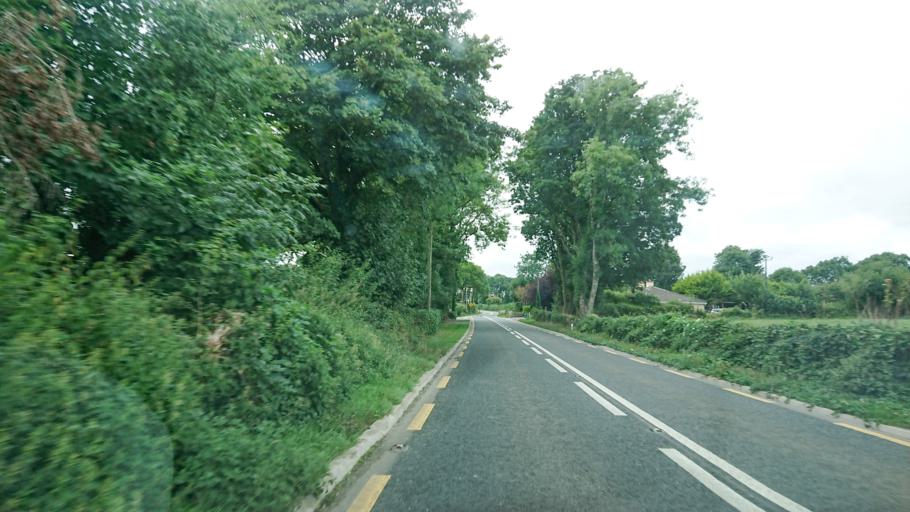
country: IE
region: Munster
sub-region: County Cork
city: Mallow
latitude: 52.1543
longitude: -8.5734
